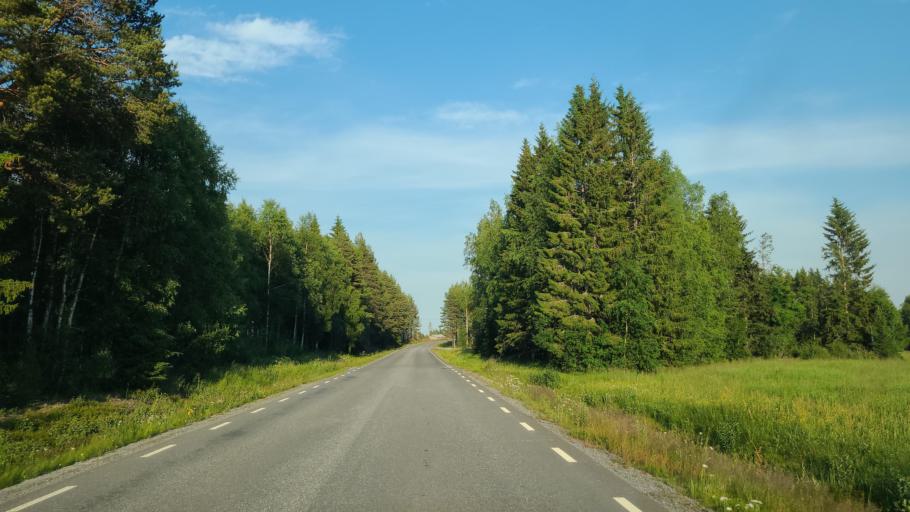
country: SE
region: Vaesterbotten
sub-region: Skelleftea Kommun
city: Burea
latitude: 64.4517
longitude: 21.4504
